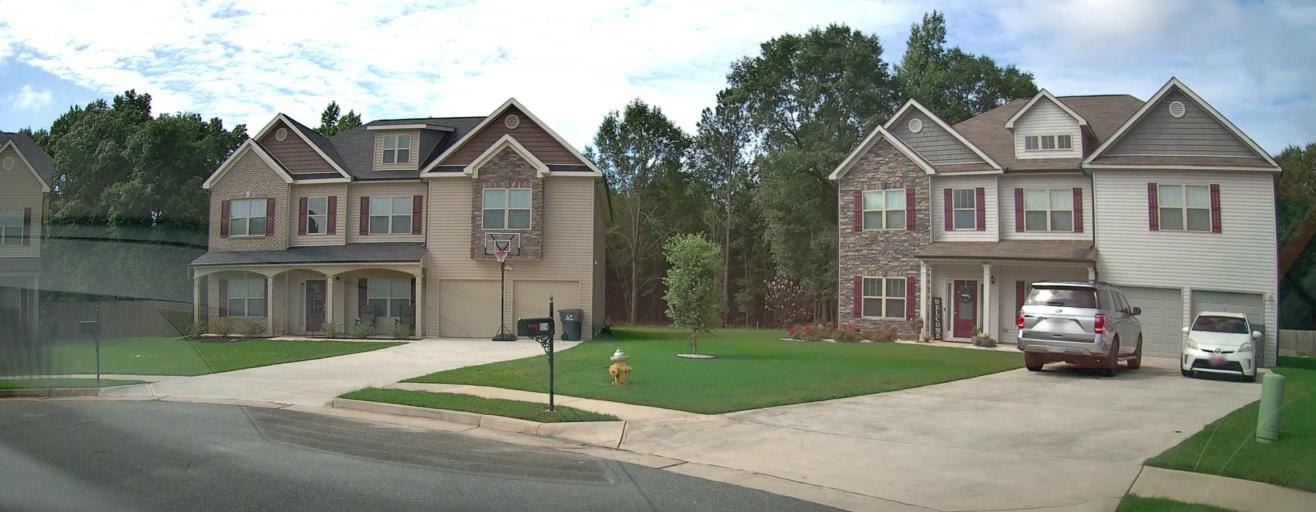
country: US
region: Georgia
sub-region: Peach County
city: Byron
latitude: 32.6273
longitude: -83.7365
